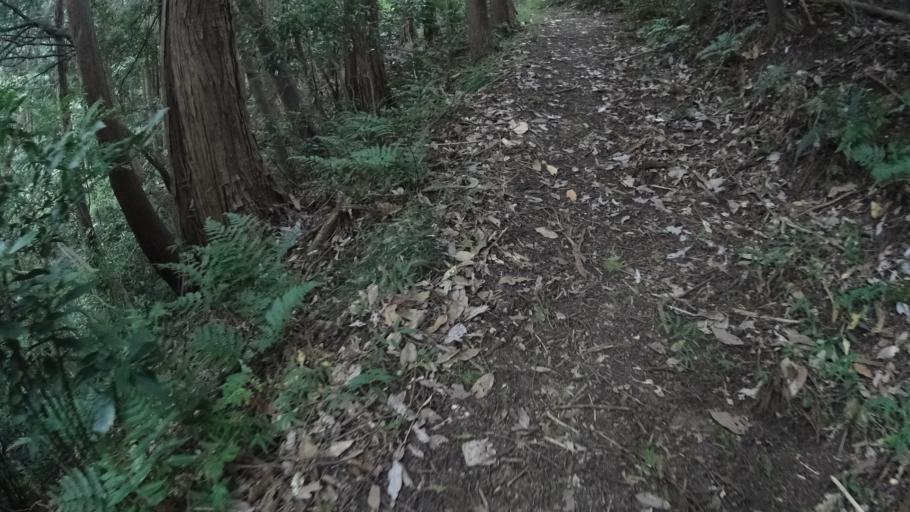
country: JP
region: Kanagawa
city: Kamakura
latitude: 35.3542
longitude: 139.5926
